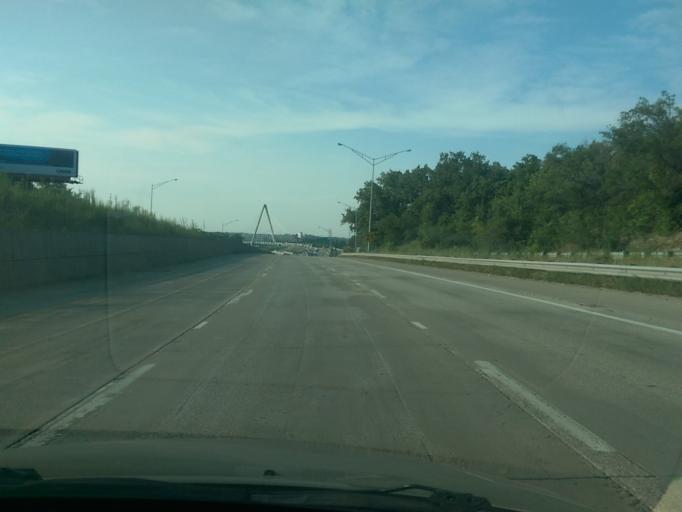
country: US
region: Missouri
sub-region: Jackson County
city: Kansas City
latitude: 39.1116
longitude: -94.5646
